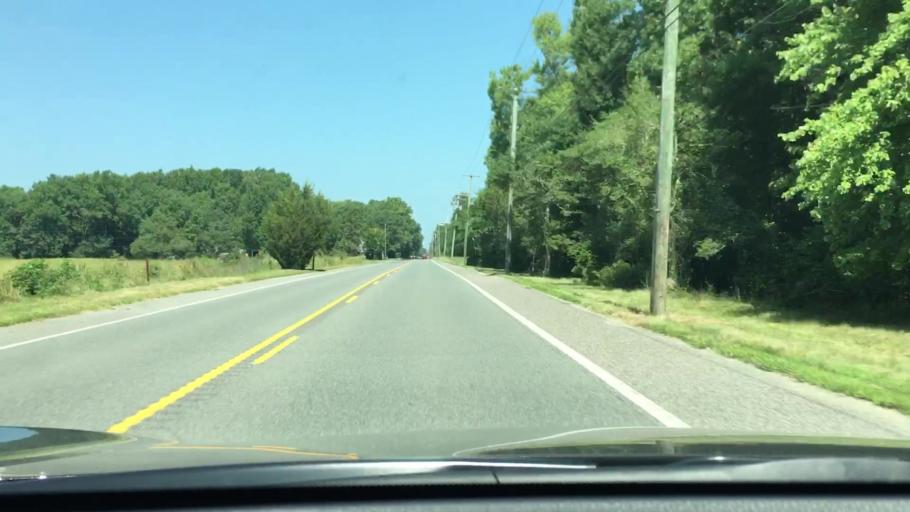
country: US
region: New Jersey
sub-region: Cumberland County
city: Laurel Lake
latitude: 39.3055
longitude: -75.0046
